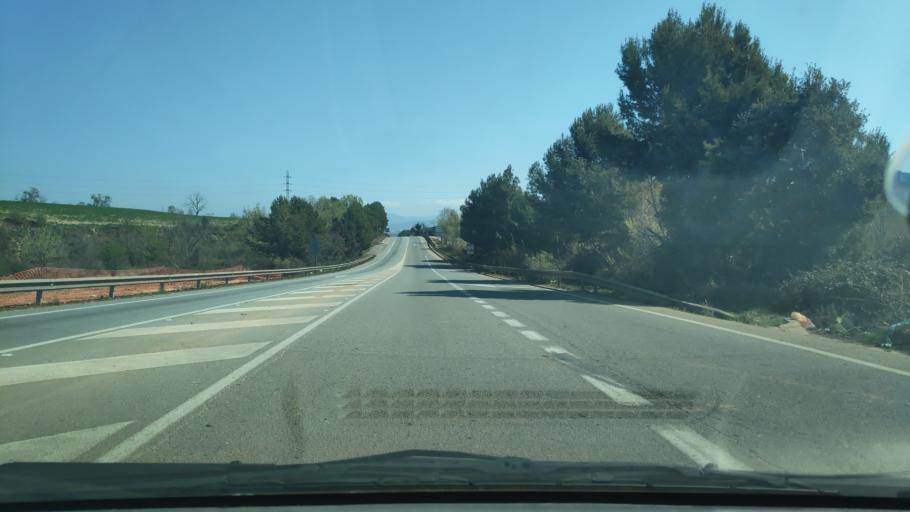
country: ES
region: Catalonia
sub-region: Provincia de Barcelona
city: Barbera del Valles
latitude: 41.5314
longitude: 2.1358
